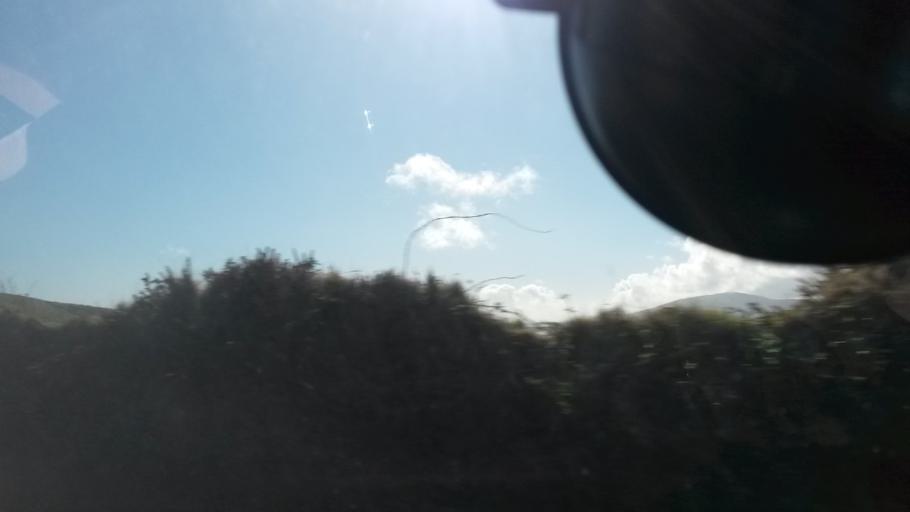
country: IE
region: Munster
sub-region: Ciarrai
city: Dingle
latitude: 52.1523
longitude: -10.2438
